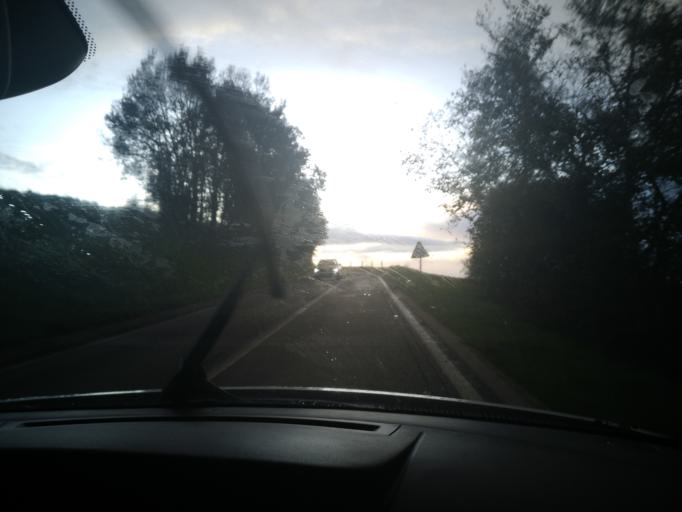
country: FR
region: Ile-de-France
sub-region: Departement des Yvelines
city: Plaisir
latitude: 48.8496
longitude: 1.9559
